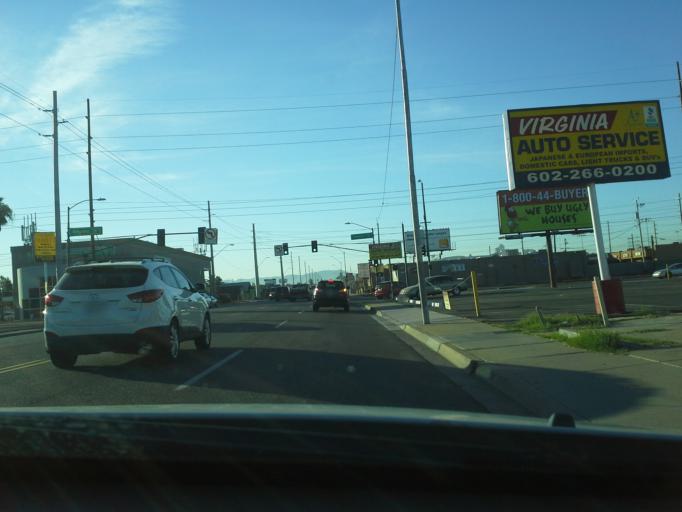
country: US
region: Arizona
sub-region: Maricopa County
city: Phoenix
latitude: 33.4772
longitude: -112.0652
